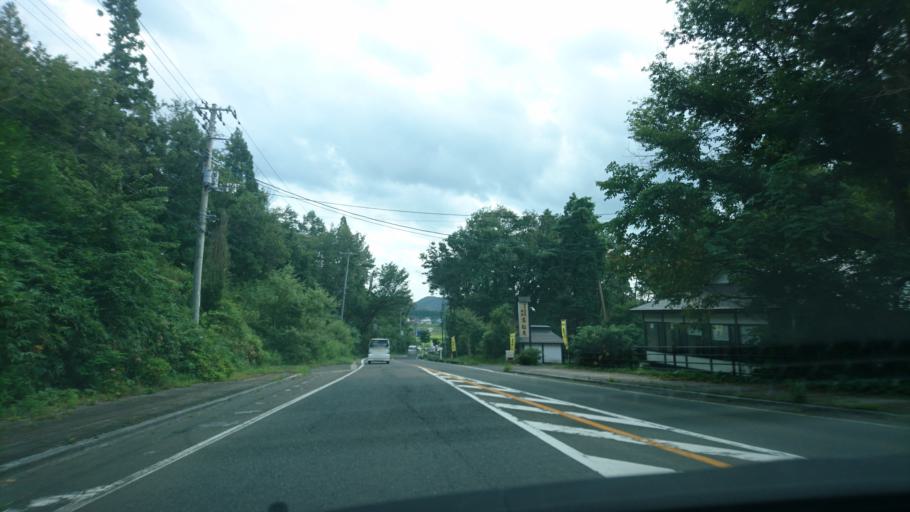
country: JP
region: Iwate
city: Hanamaki
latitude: 39.3964
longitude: 141.1653
